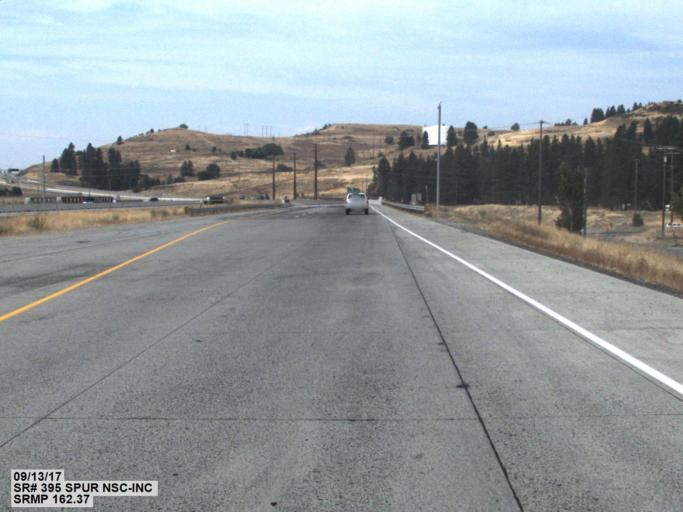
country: US
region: Washington
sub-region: Franklin County
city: Pasco
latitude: 46.2650
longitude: -119.0843
